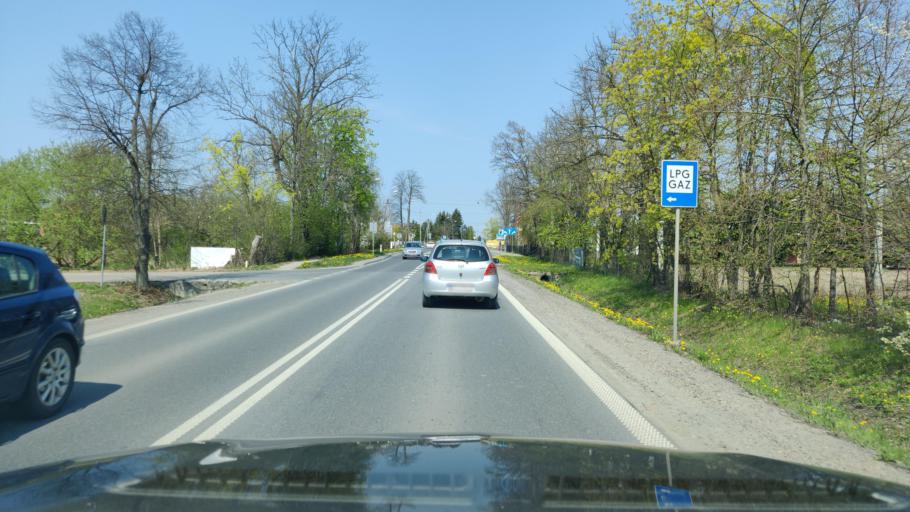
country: PL
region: Masovian Voivodeship
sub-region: Powiat pultuski
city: Pultusk
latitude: 52.6889
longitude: 21.0806
